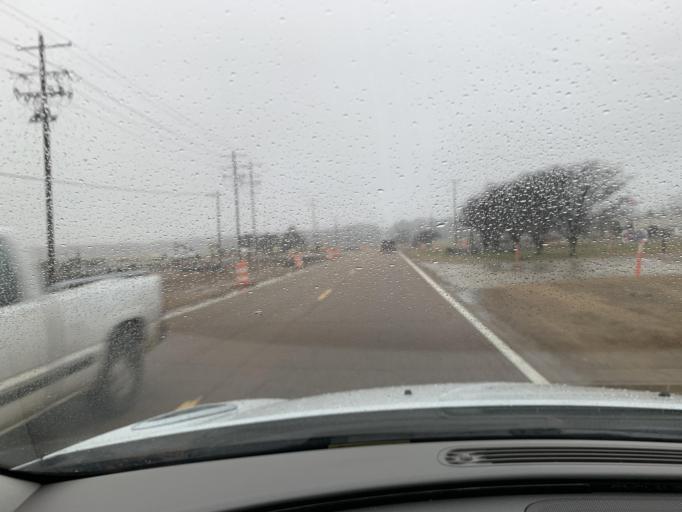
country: US
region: Mississippi
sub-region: De Soto County
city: Hernando
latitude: 34.8663
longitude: -89.9954
